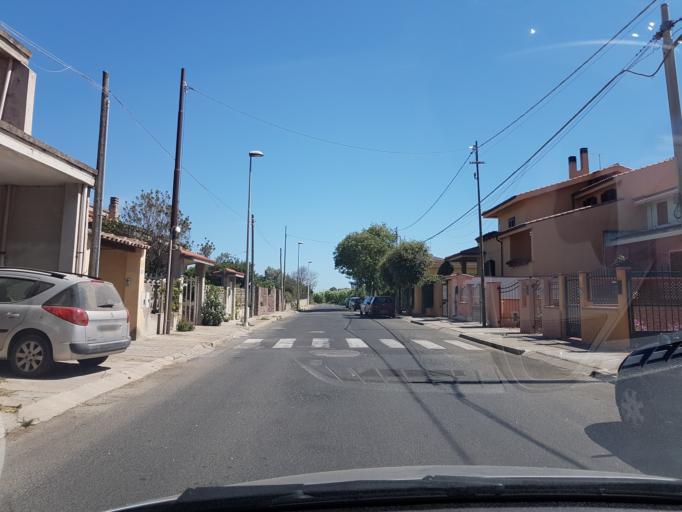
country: IT
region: Sardinia
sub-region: Provincia di Oristano
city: Cabras
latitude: 39.9224
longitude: 8.5348
